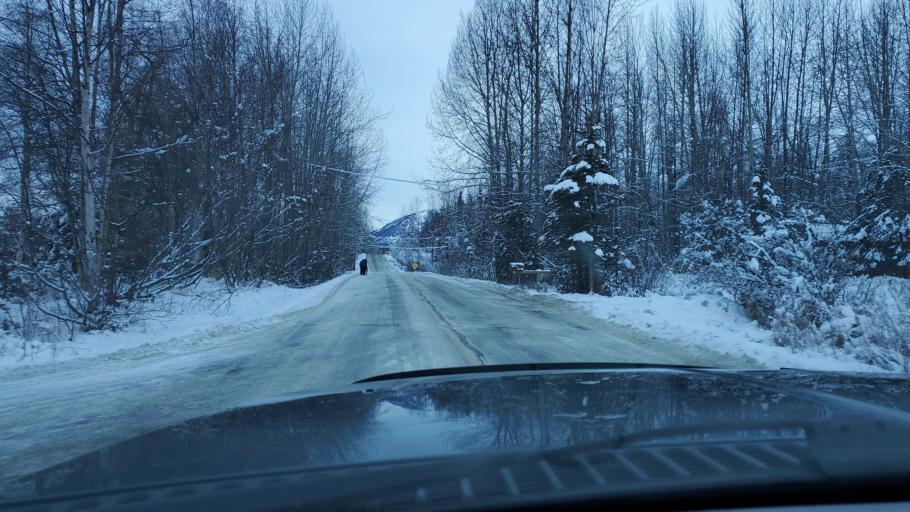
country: US
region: Alaska
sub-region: Matanuska-Susitna Borough
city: Lakes
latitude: 61.6933
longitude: -149.3073
